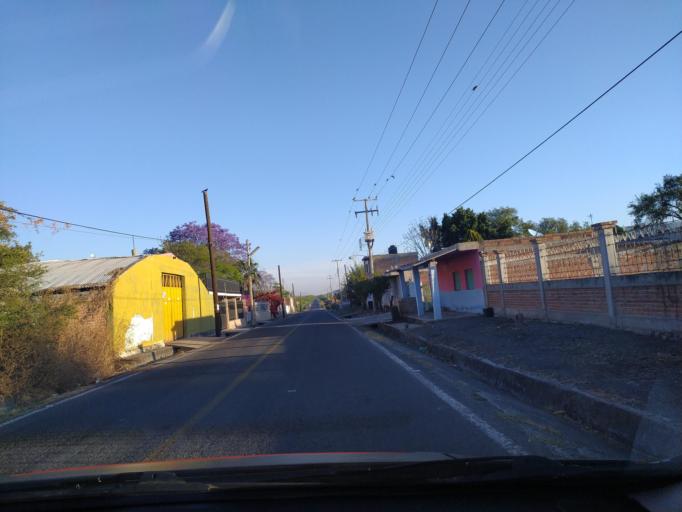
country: MX
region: Guanajuato
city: Ciudad Manuel Doblado
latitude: 20.7502
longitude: -101.8249
